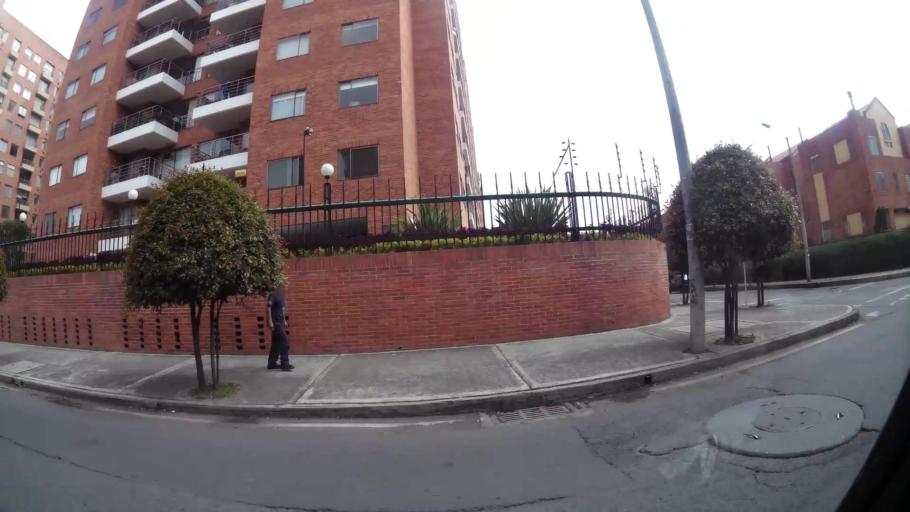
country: CO
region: Bogota D.C.
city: Barrio San Luis
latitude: 4.7342
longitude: -74.0579
